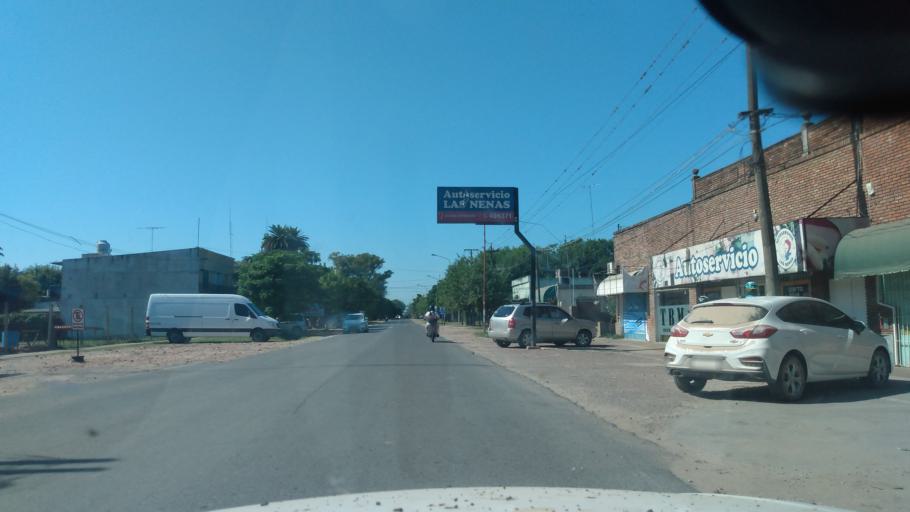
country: AR
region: Buenos Aires
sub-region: Partido de Lujan
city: Lujan
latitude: -34.4908
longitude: -59.0779
